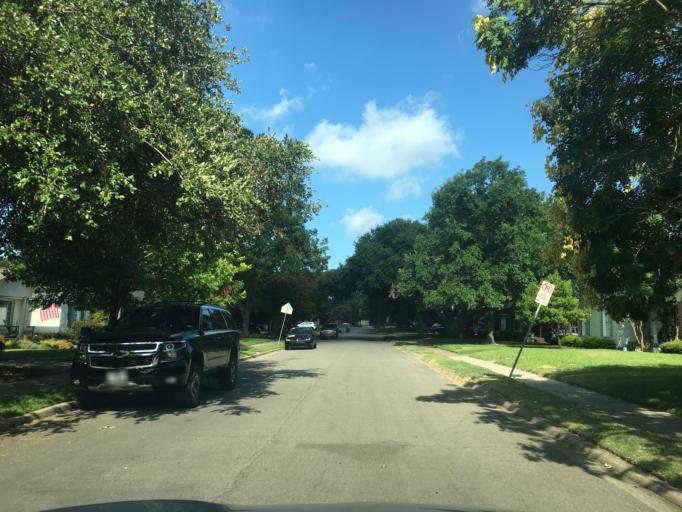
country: US
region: Texas
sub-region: Dallas County
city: Highland Park
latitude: 32.8329
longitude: -96.7556
